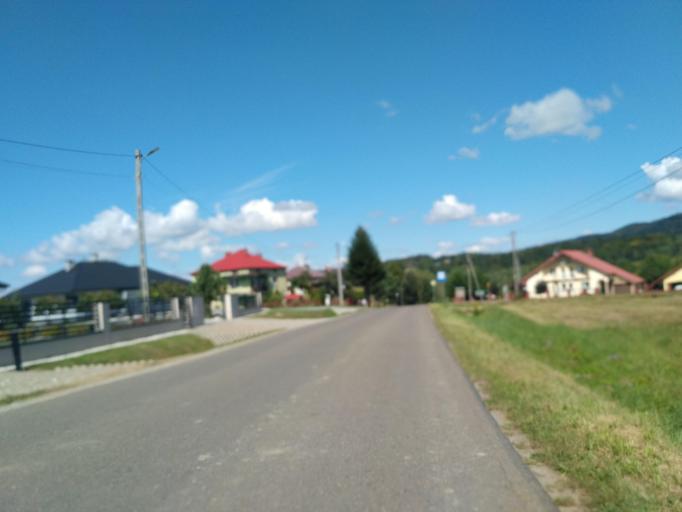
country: PL
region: Subcarpathian Voivodeship
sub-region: Powiat jasielski
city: Skolyszyn
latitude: 49.7873
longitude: 21.3429
